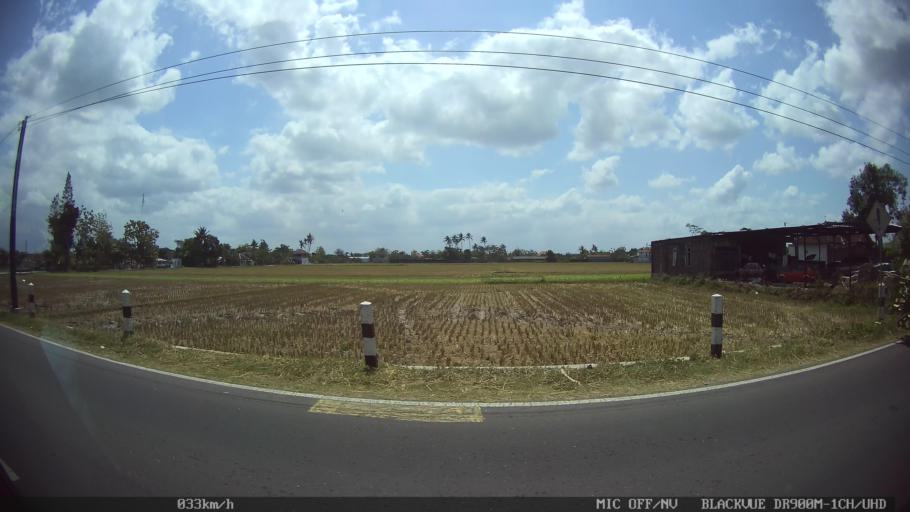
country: ID
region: Daerah Istimewa Yogyakarta
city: Sewon
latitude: -7.9127
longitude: 110.3619
